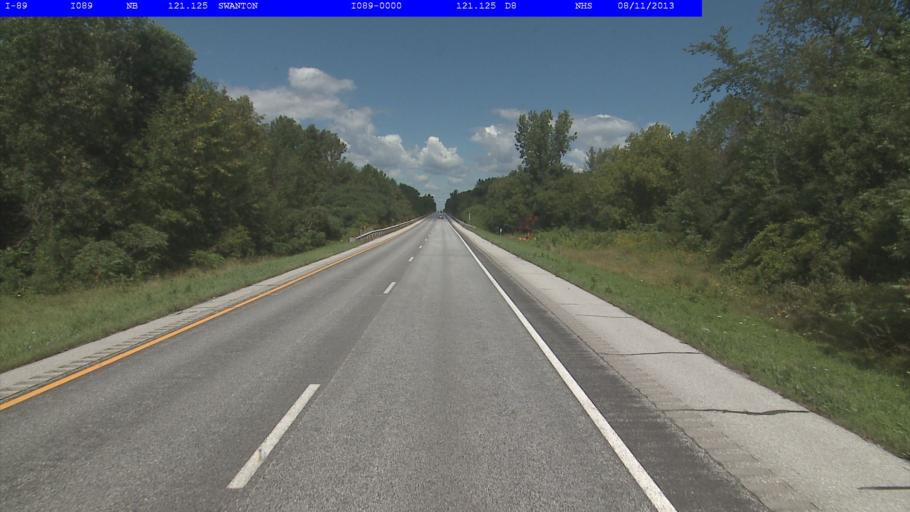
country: US
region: Vermont
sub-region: Franklin County
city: Swanton
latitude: 44.8929
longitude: -73.0880
